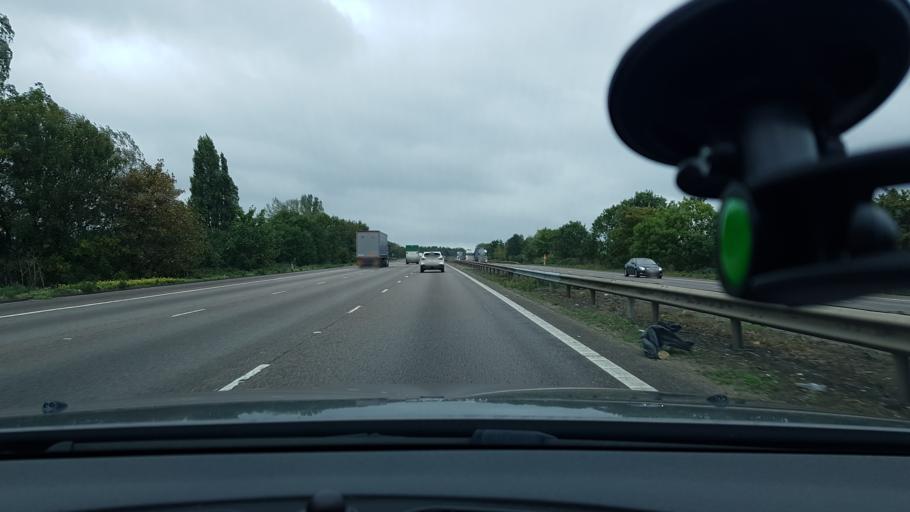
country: GB
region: England
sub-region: Essex
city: Epping
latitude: 51.7149
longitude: 0.1442
